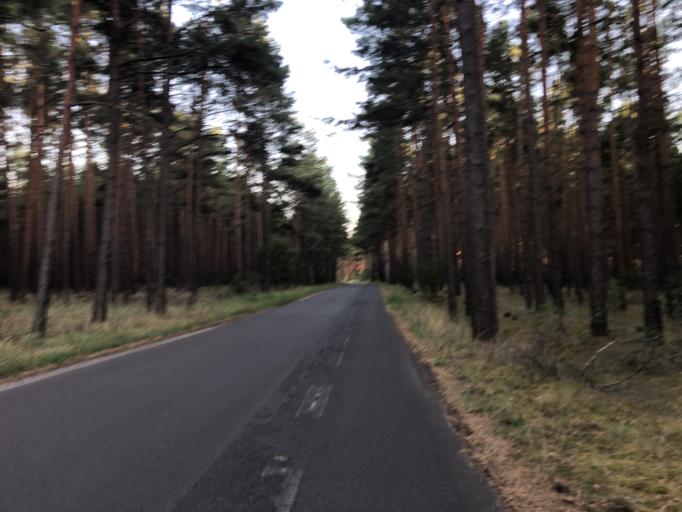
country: DE
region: Brandenburg
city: Mullrose
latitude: 52.2579
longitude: 14.4776
